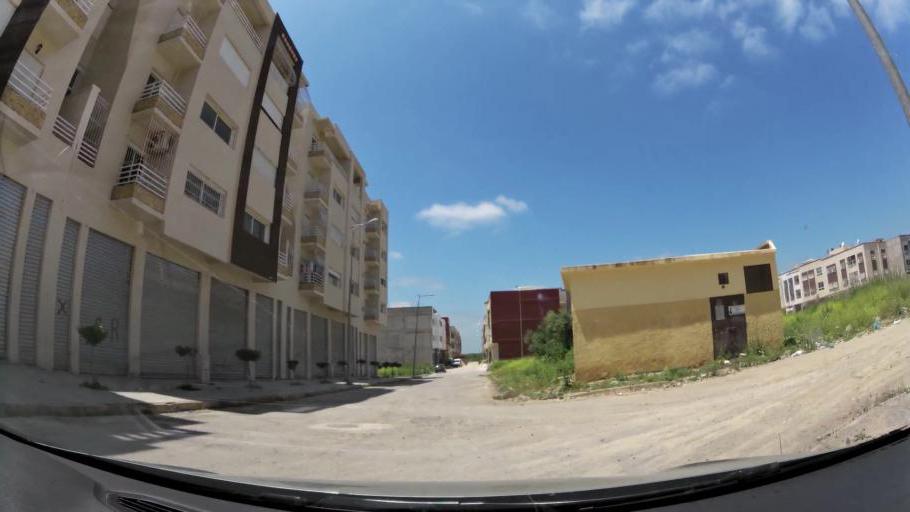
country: MA
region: Fes-Boulemane
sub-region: Fes
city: Fes
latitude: 34.0499
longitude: -5.0408
